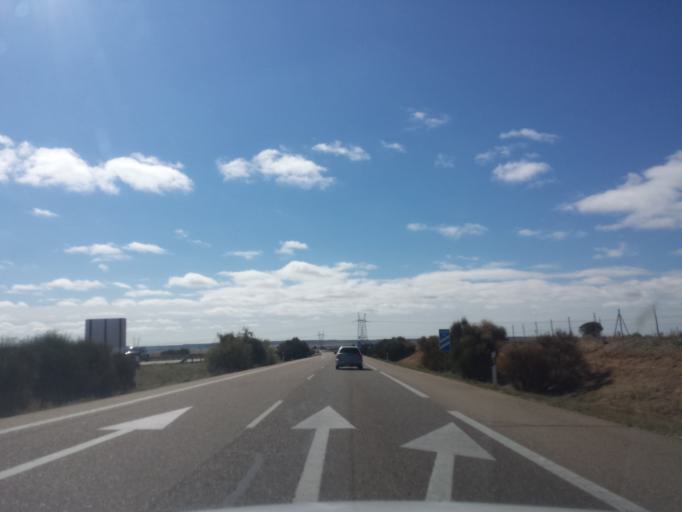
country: ES
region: Castille and Leon
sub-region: Provincia de Valladolid
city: San Pedro de Latarce
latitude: 41.7623
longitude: -5.2958
